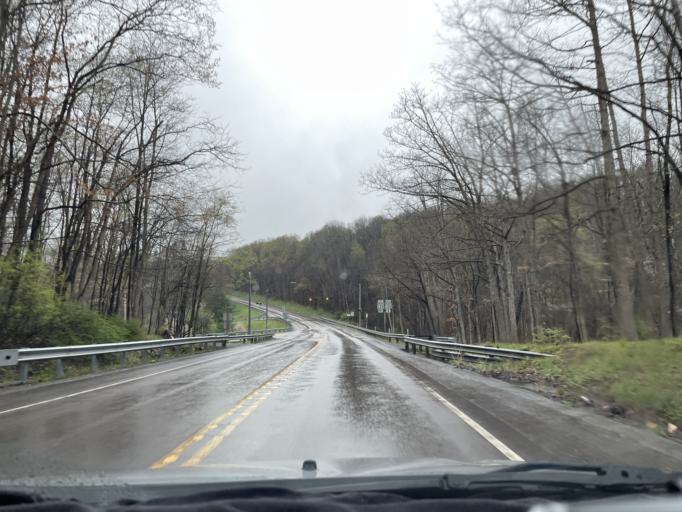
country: US
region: Maryland
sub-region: Garrett County
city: Mountain Lake Park
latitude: 39.4369
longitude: -79.2856
